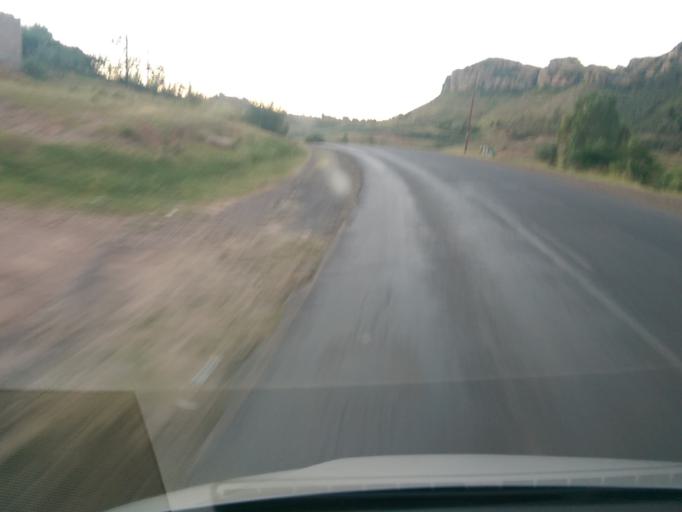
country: LS
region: Maseru
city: Nako
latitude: -29.4373
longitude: 27.7014
